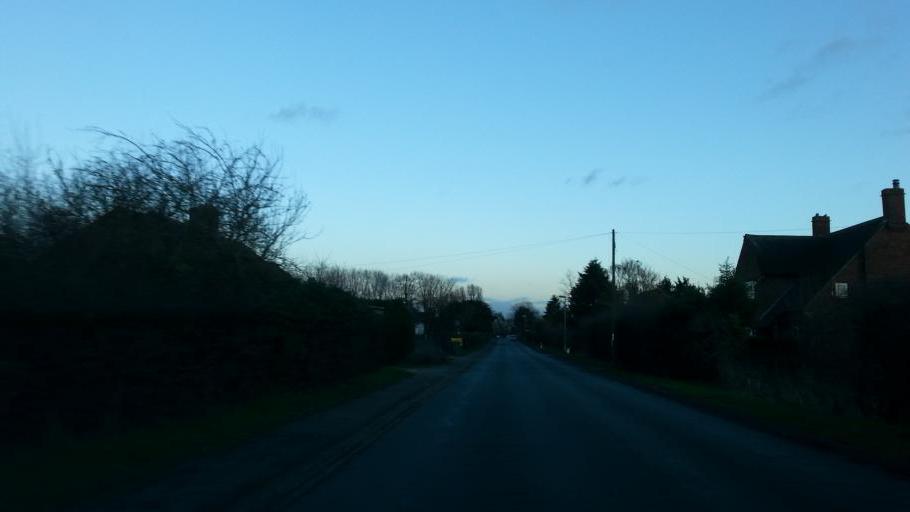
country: GB
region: England
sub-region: Cambridgeshire
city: Needingworth
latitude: 52.2986
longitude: -0.0459
